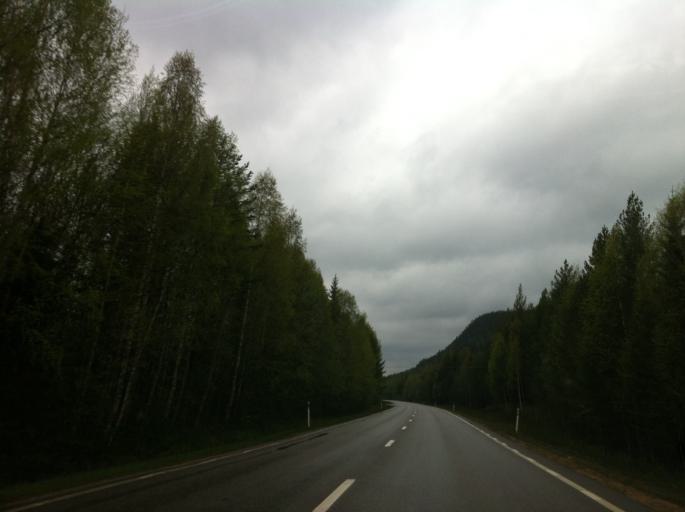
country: SE
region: Jaemtland
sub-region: Harjedalens Kommun
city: Sveg
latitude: 62.0958
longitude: 14.2344
